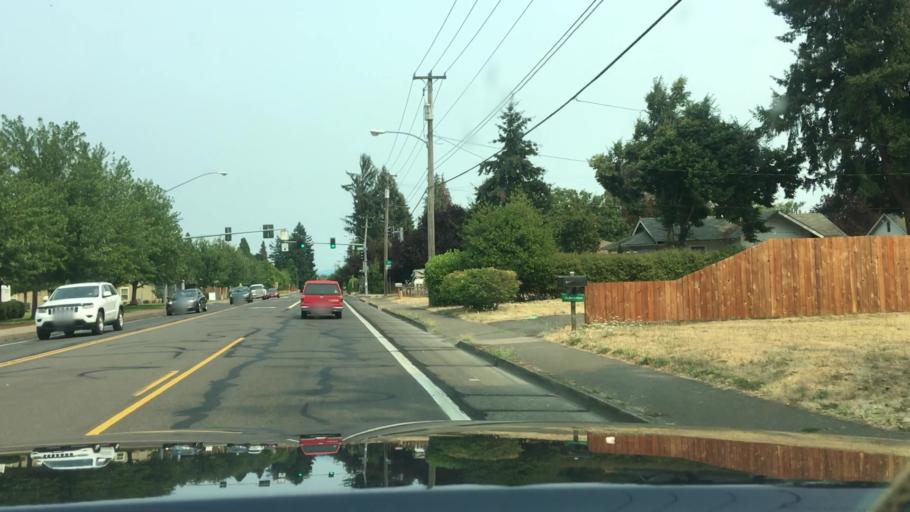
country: US
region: Oregon
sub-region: Lane County
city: Eugene
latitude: 44.0845
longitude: -123.1617
